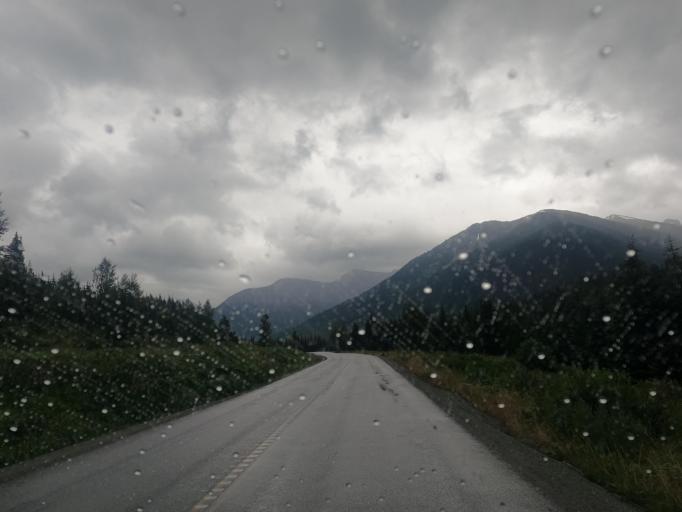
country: CA
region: British Columbia
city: Pemberton
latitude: 50.3827
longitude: -122.4234
